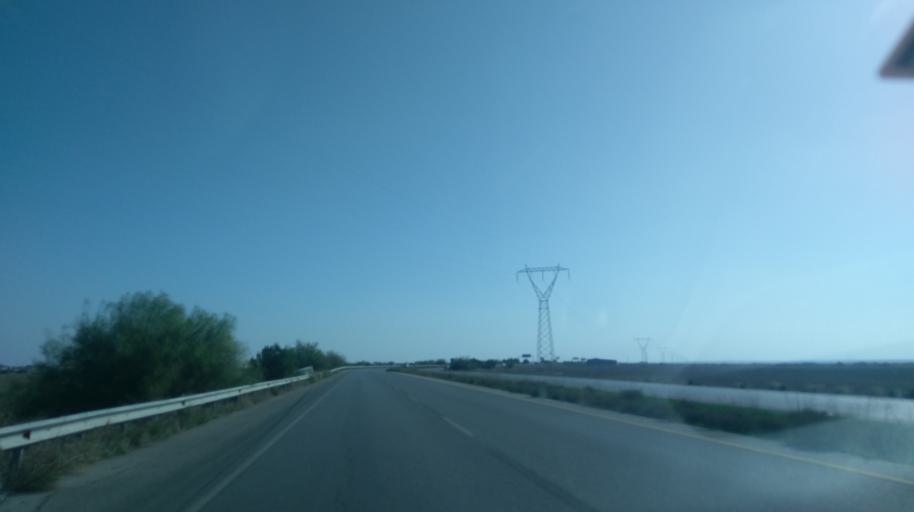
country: CY
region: Ammochostos
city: Acheritou
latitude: 35.1709
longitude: 33.8152
